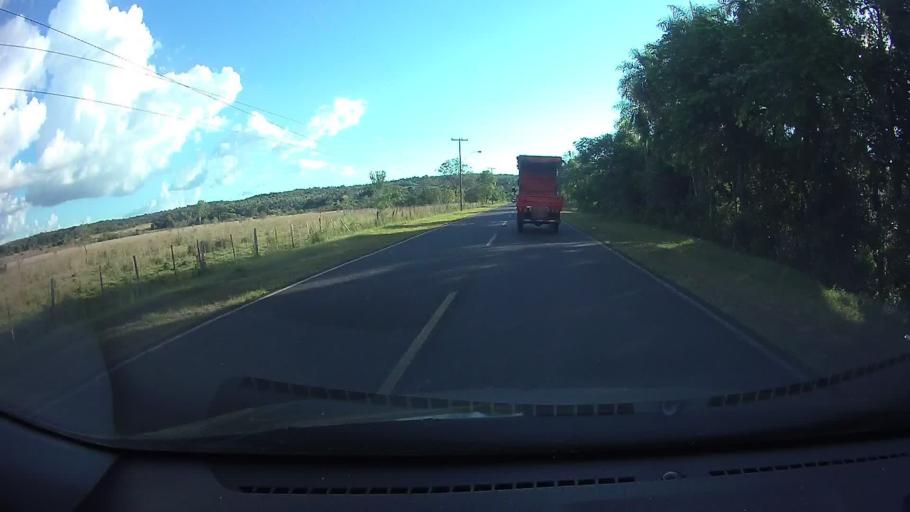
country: PY
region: Cordillera
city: Emboscada
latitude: -25.1626
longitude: -57.2668
